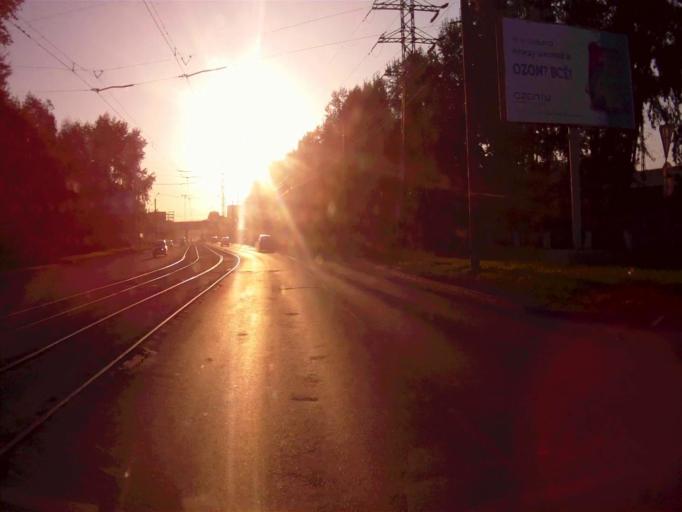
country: RU
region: Chelyabinsk
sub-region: Gorod Chelyabinsk
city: Chelyabinsk
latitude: 55.1683
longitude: 61.4333
